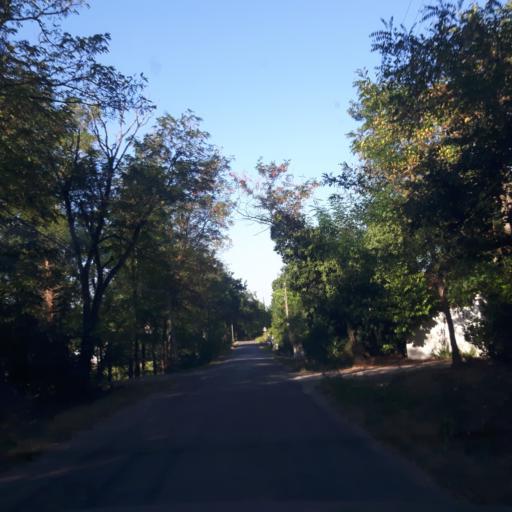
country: FR
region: Midi-Pyrenees
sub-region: Departement de la Haute-Garonne
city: Bouloc
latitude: 43.7959
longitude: 1.4167
